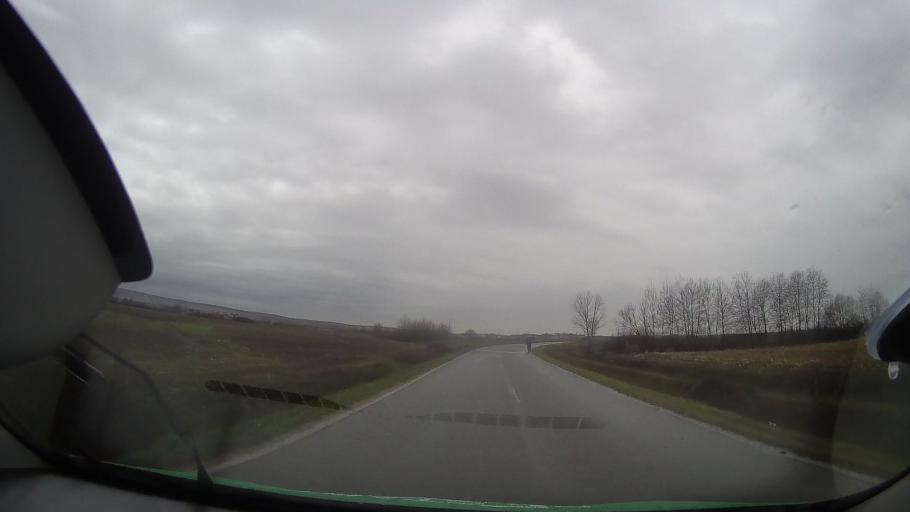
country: RO
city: Capalna
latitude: 46.7131
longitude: 22.0648
